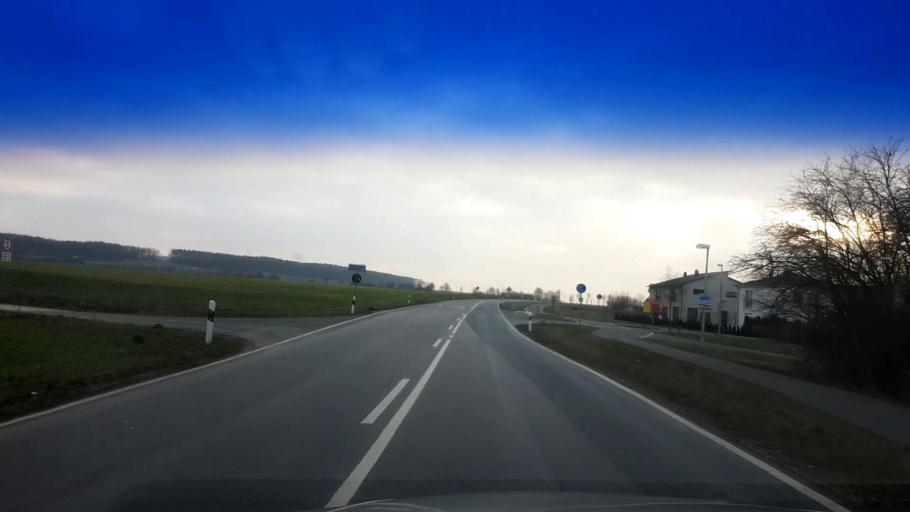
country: DE
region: Bavaria
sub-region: Upper Franconia
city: Hirschaid
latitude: 49.8011
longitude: 10.9731
